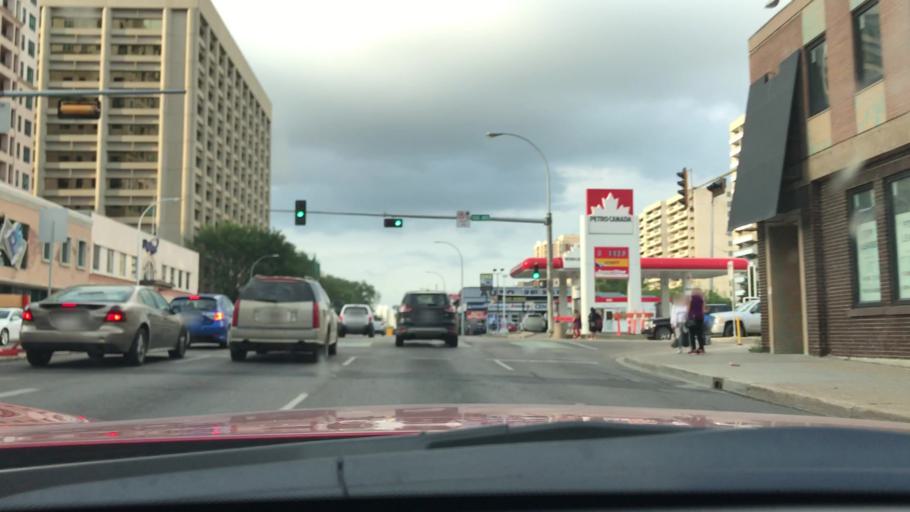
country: CA
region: Alberta
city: Edmonton
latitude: 53.5391
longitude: -113.5086
